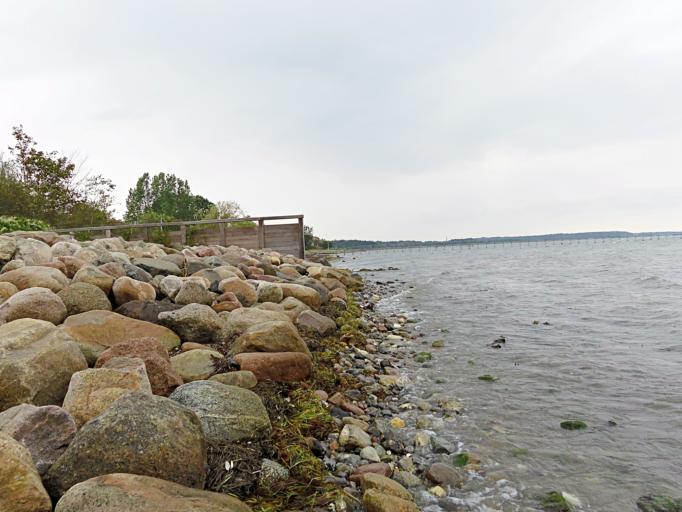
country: DK
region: Capital Region
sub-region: Fredensborg Kommune
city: Kokkedal
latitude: 55.9124
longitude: 12.5238
